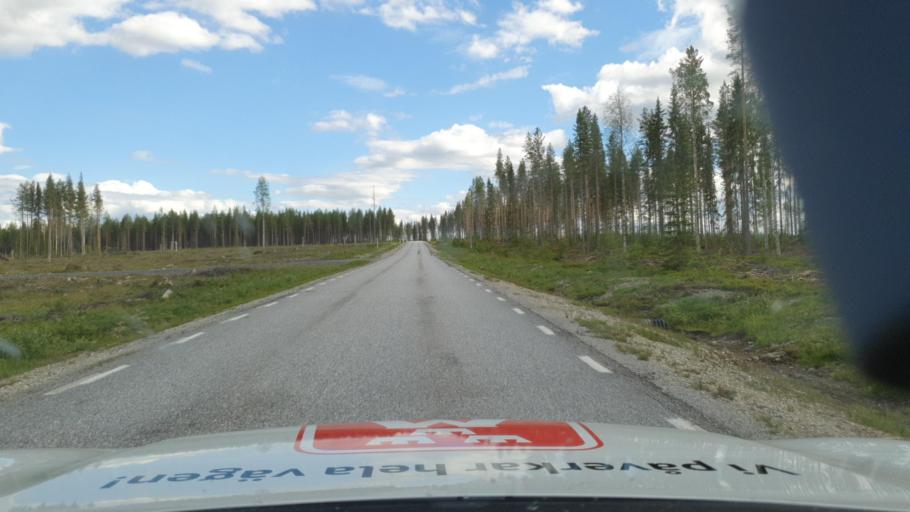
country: SE
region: Vaesterbotten
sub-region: Skelleftea Kommun
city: Langsele
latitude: 64.7036
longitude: 19.9918
